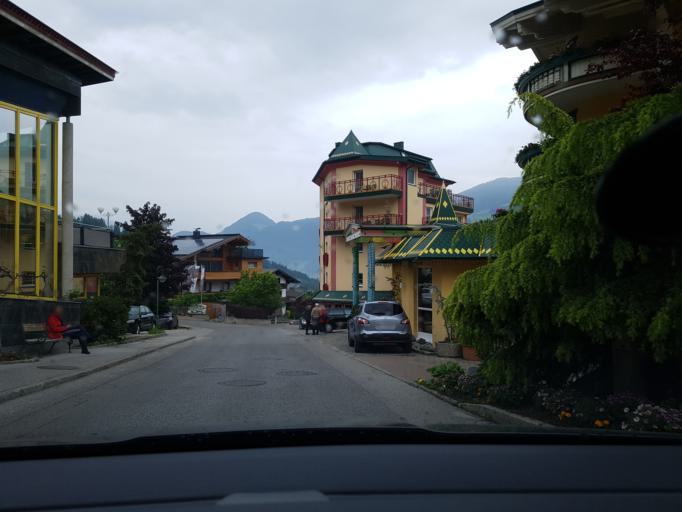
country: AT
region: Tyrol
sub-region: Politischer Bezirk Schwaz
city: Fugen
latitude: 47.3396
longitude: 11.8438
